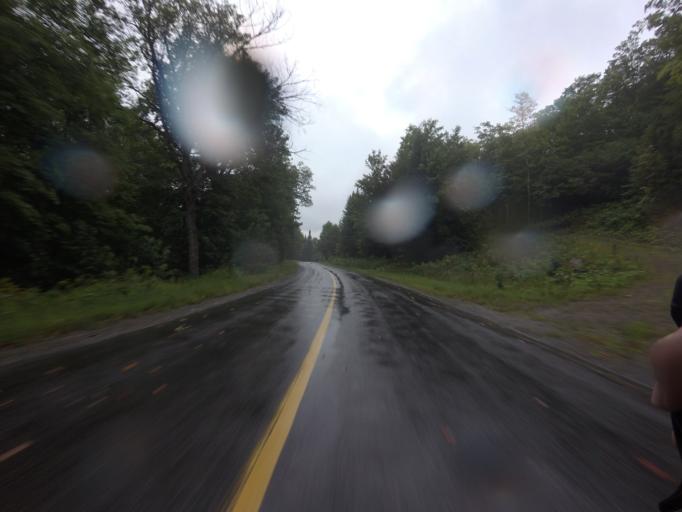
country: CA
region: Ontario
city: Perth
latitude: 45.0587
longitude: -76.6128
